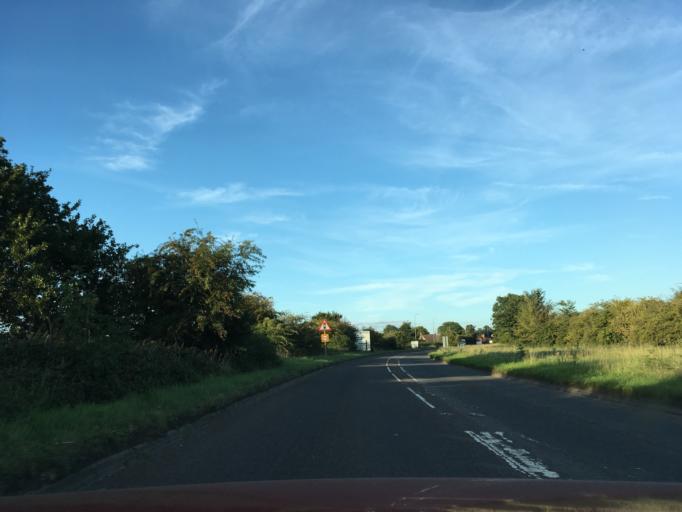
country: GB
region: England
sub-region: South Gloucestershire
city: Tytherington
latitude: 51.5512
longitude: -2.4714
